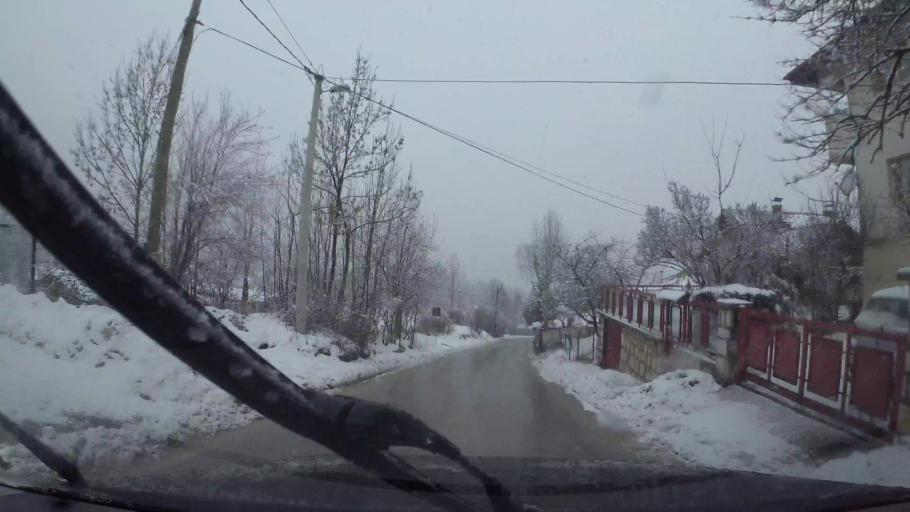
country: BA
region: Federation of Bosnia and Herzegovina
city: Kobilja Glava
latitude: 43.8534
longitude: 18.4408
